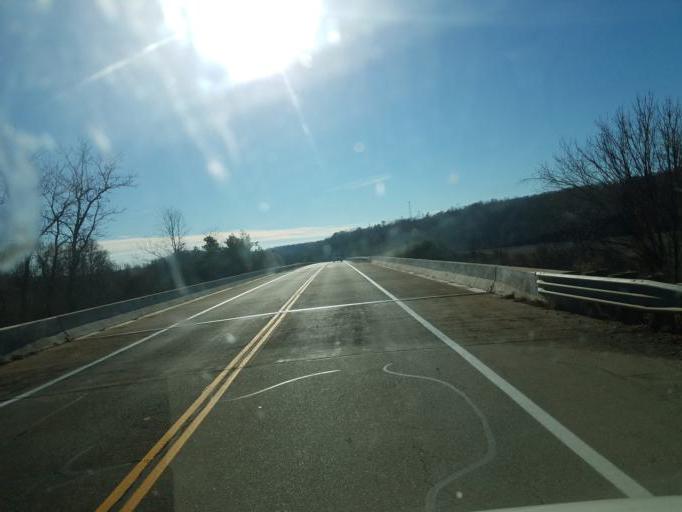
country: US
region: Ohio
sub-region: Muskingum County
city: Dresden
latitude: 40.1411
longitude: -82.0292
